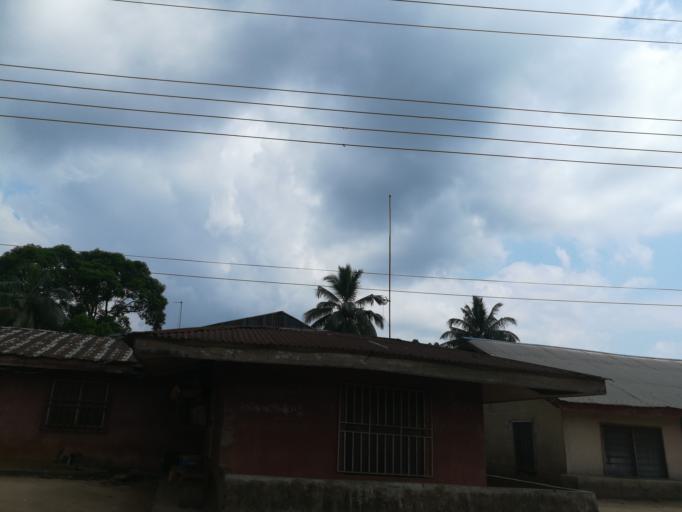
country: NG
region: Rivers
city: Okrika
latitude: 4.7286
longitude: 7.1486
